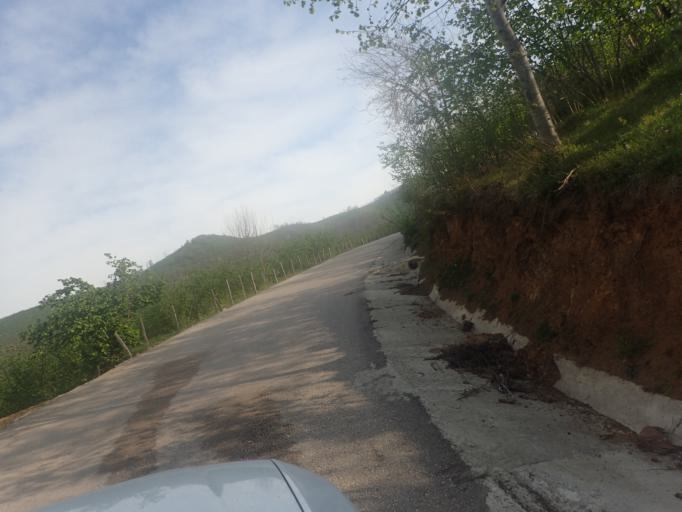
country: TR
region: Ordu
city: Catalpinar
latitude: 40.8793
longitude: 37.4738
